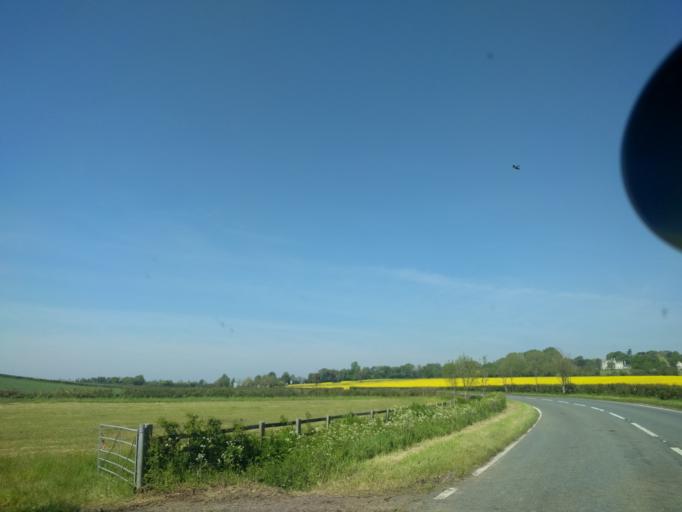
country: GB
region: England
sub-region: Somerset
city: Ilchester
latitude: 51.0264
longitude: -2.6811
